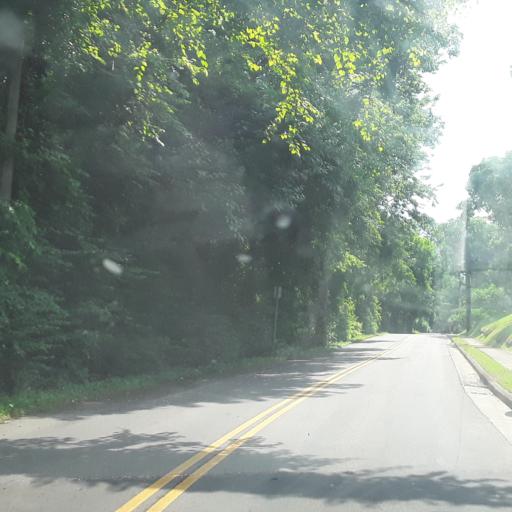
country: US
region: Tennessee
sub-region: Davidson County
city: Oak Hill
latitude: 36.1161
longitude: -86.7339
